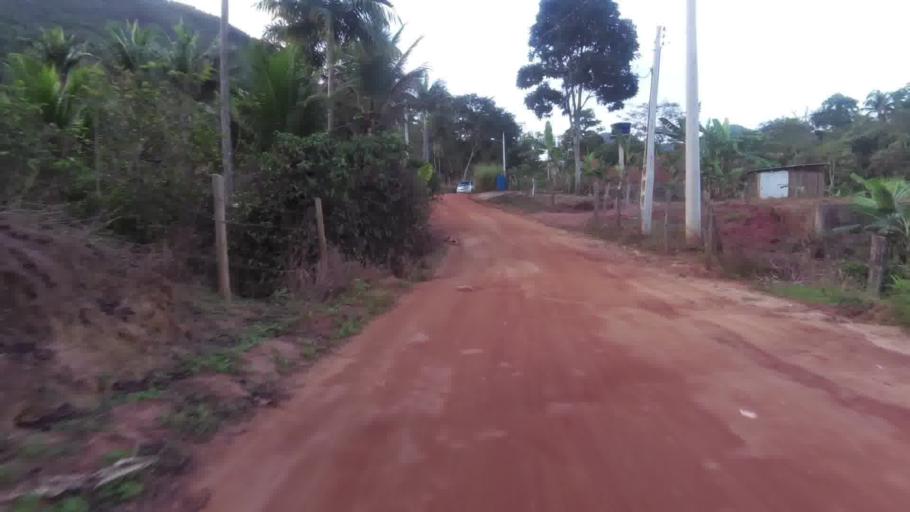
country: BR
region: Espirito Santo
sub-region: Guarapari
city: Guarapari
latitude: -20.6728
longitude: -40.6144
